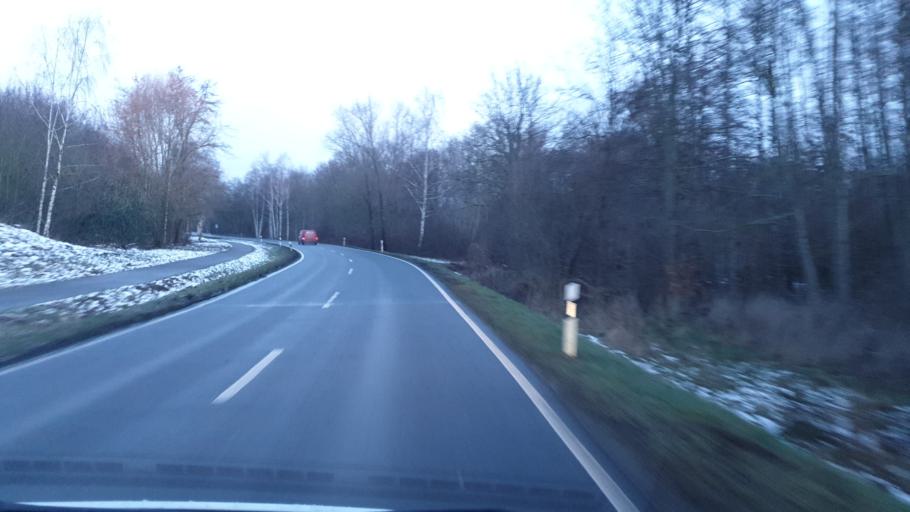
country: DE
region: Saxony
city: Markkleeberg
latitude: 51.2906
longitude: 12.3572
